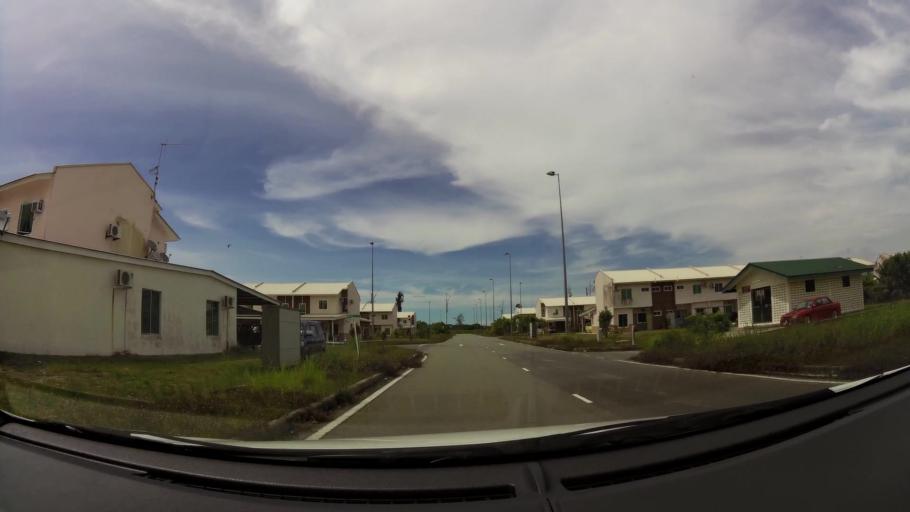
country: BN
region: Belait
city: Kuala Belait
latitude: 4.5921
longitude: 114.2786
